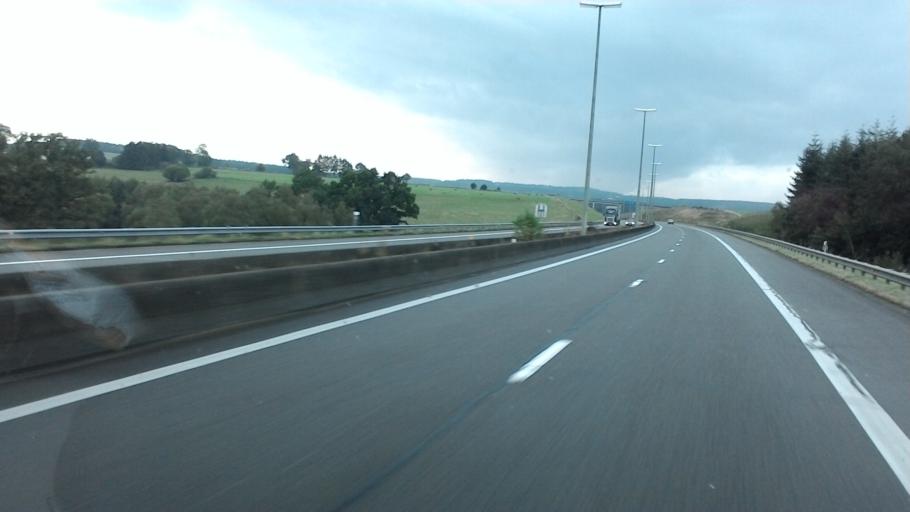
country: BE
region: Wallonia
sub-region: Province du Luxembourg
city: Houffalize
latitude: 50.1542
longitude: 5.7930
